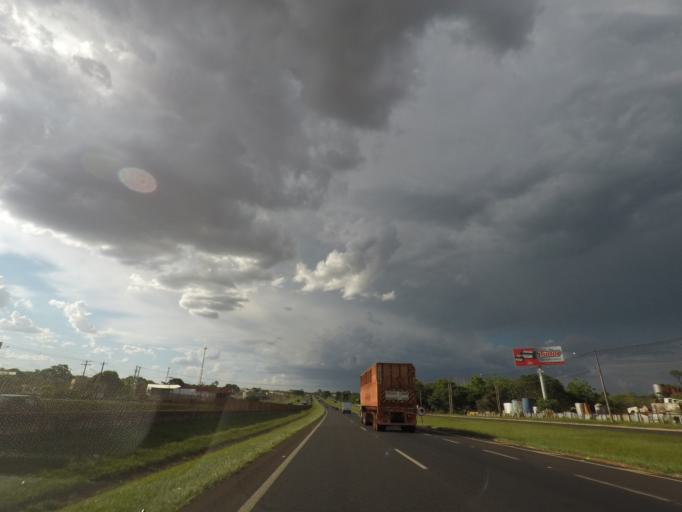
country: BR
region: Sao Paulo
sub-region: Ribeirao Preto
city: Ribeirao Preto
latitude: -21.1352
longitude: -47.7642
